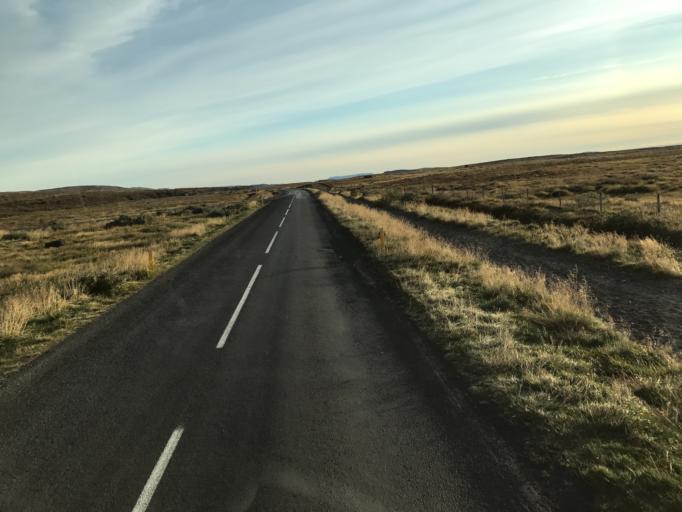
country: IS
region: South
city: Vestmannaeyjar
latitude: 64.3257
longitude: -20.1314
